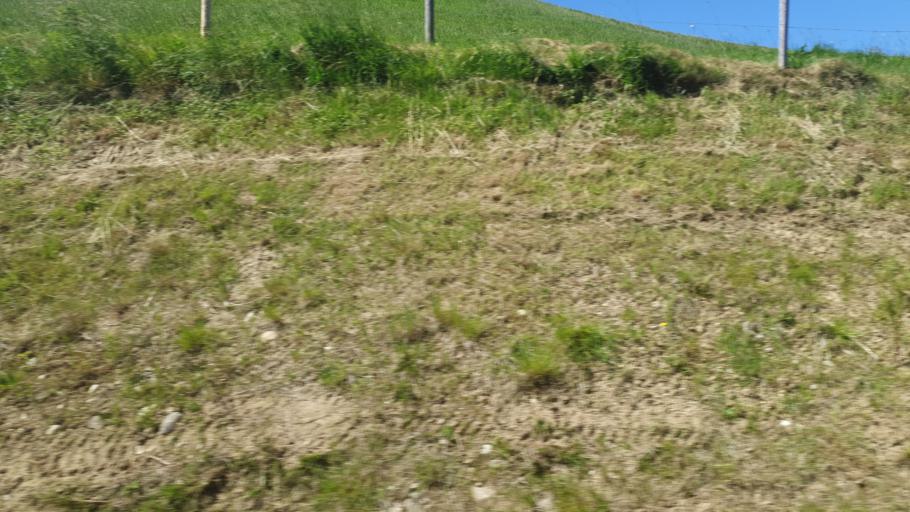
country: CH
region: Fribourg
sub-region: Sarine District
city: Givisiez
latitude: 46.8483
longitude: 7.1370
